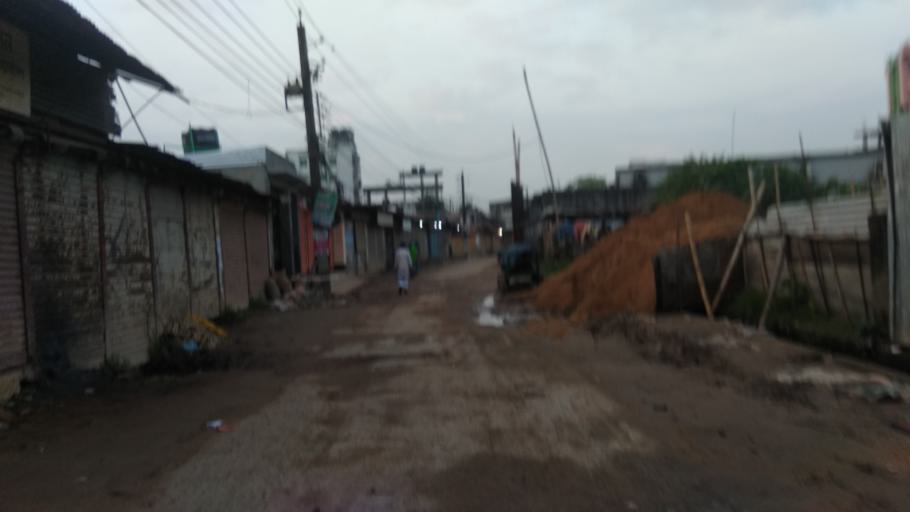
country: BD
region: Dhaka
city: Tungi
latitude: 23.8530
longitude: 90.4265
